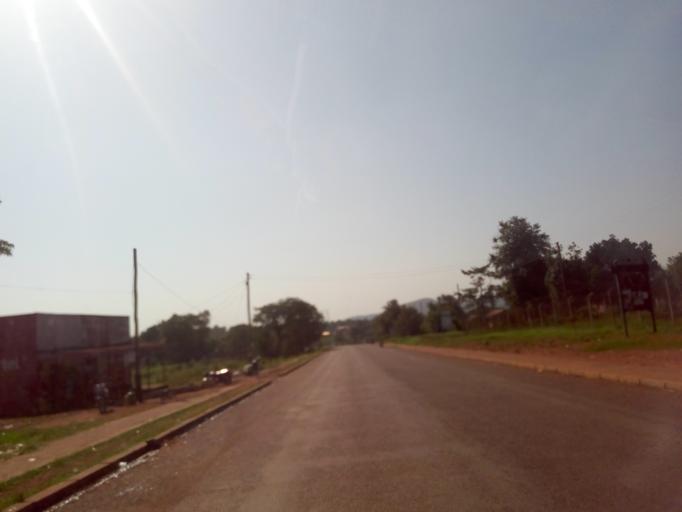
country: UG
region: Western Region
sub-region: Masindi District
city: Masindi
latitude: 1.6813
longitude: 31.7259
